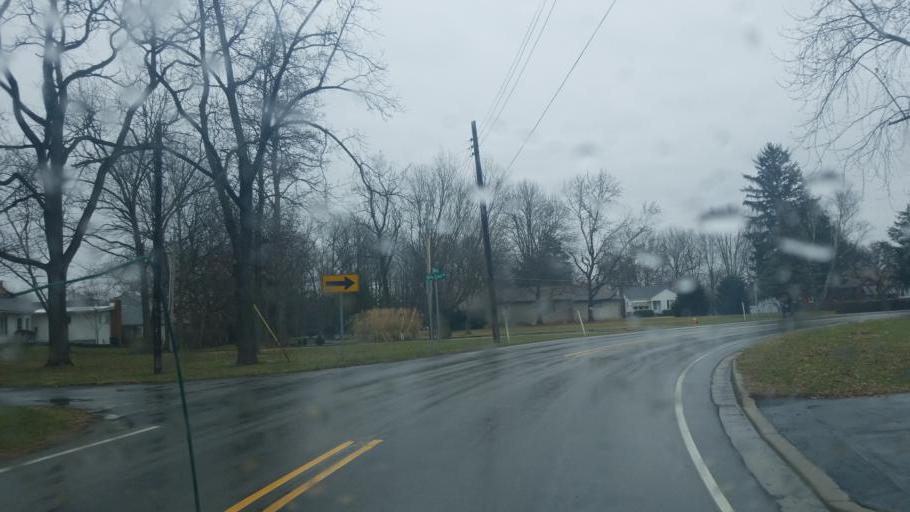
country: US
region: Indiana
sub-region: Shelby County
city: Shelbyville
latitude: 39.5098
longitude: -85.7716
